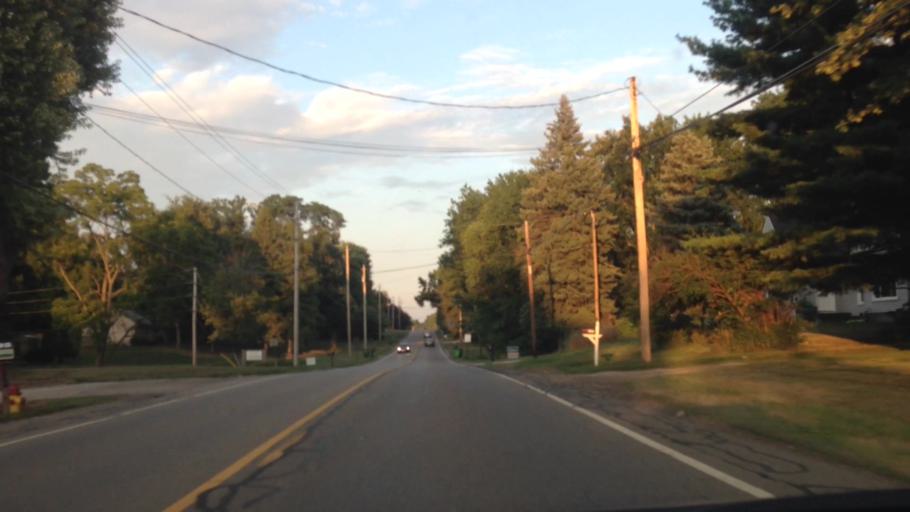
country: US
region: Ohio
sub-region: Summit County
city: Green
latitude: 40.9744
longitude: -81.4848
